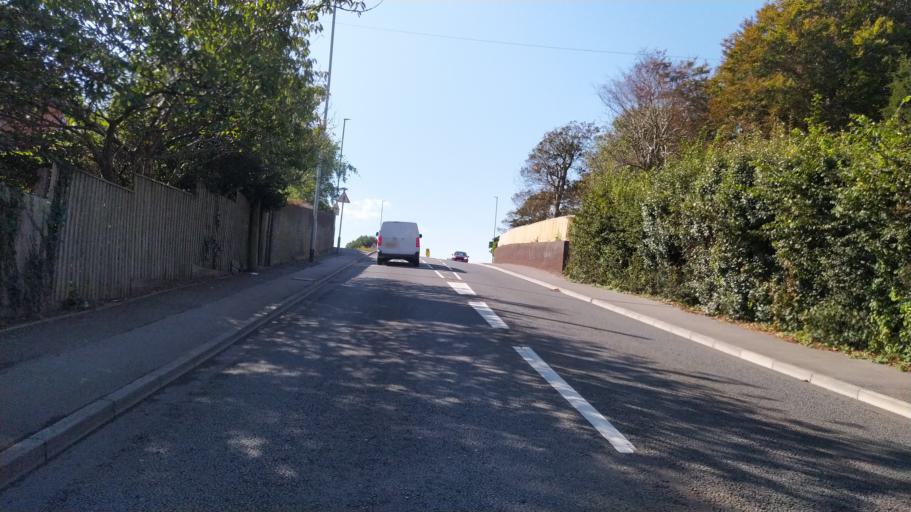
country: GB
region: England
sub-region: Dorset
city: Weymouth
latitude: 50.5988
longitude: -2.4705
